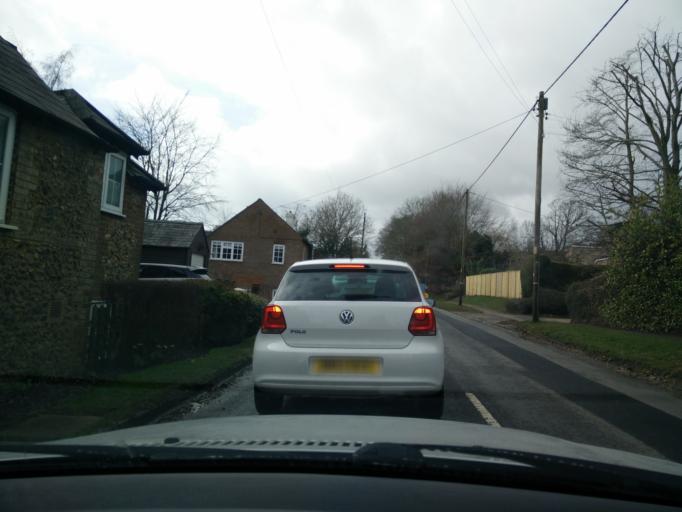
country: GB
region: England
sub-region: Buckinghamshire
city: Great Missenden
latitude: 51.6832
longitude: -0.6963
